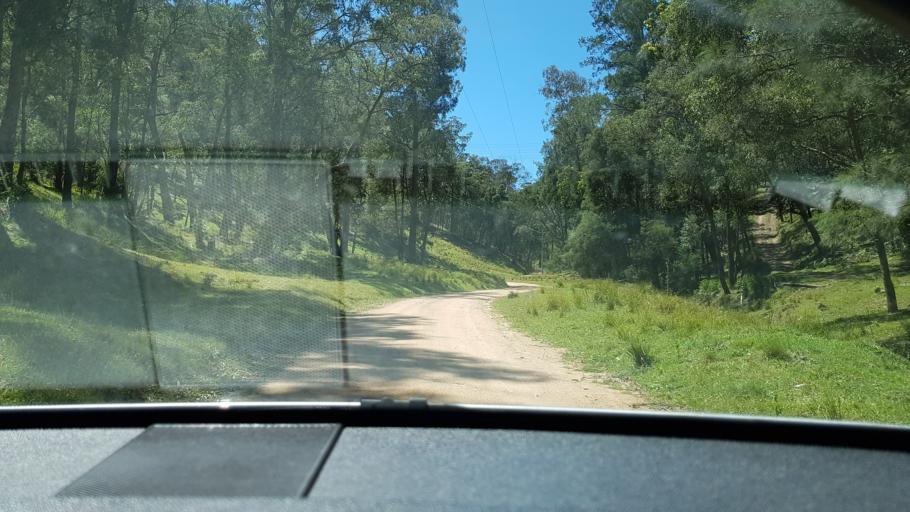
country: AU
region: New South Wales
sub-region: Blue Mountains Municipality
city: Katoomba
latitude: -33.7792
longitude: 150.2330
